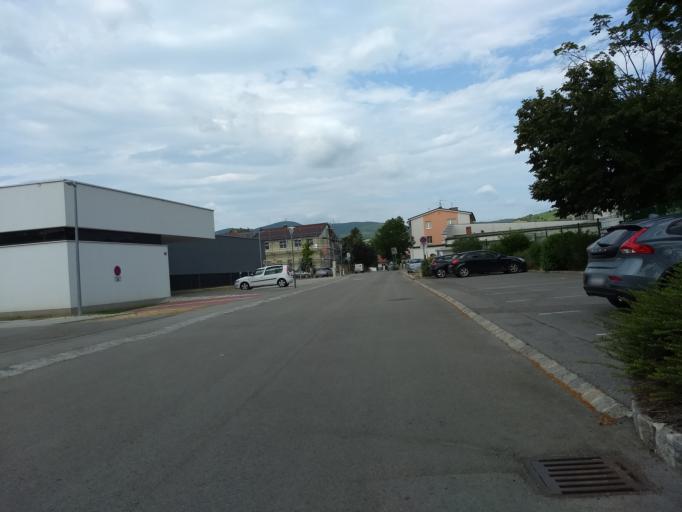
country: AT
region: Lower Austria
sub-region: Politischer Bezirk Modling
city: Guntramsdorf
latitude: 48.0523
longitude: 16.3164
